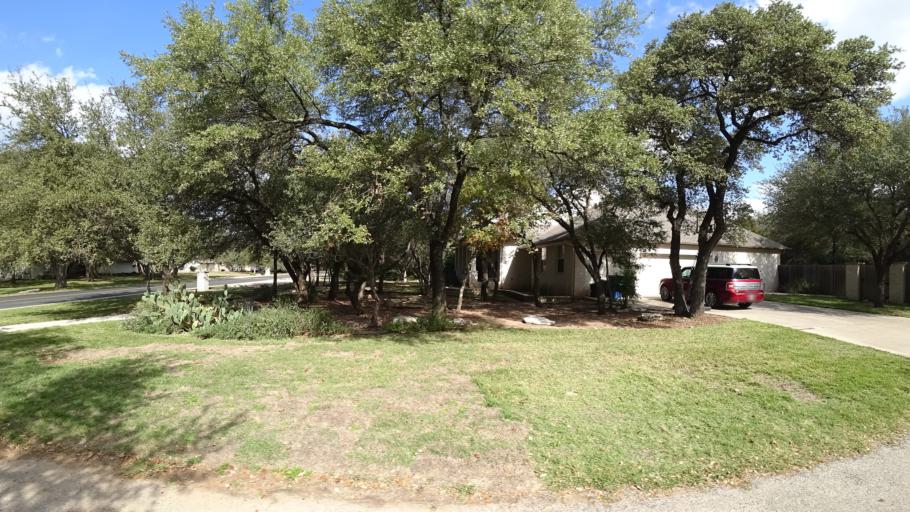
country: US
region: Texas
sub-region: Williamson County
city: Jollyville
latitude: 30.4171
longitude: -97.7812
